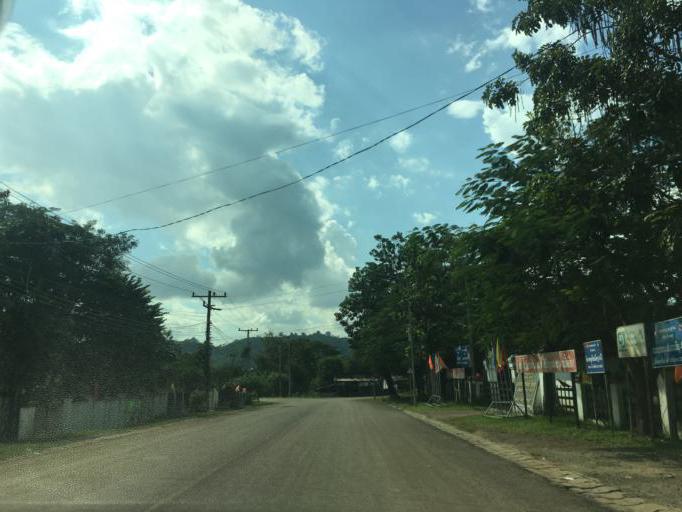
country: TH
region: Nong Khai
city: Sangkhom
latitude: 18.2174
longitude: 102.2354
